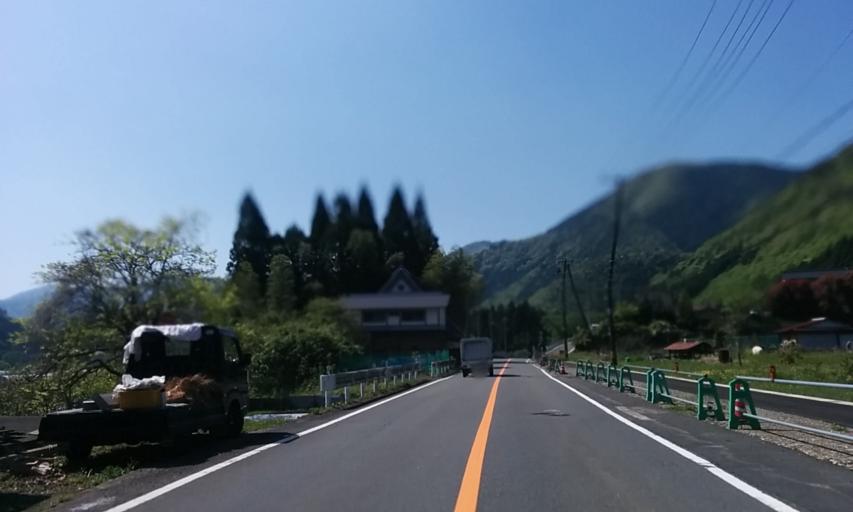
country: JP
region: Kyoto
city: Maizuru
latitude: 35.2758
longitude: 135.5446
